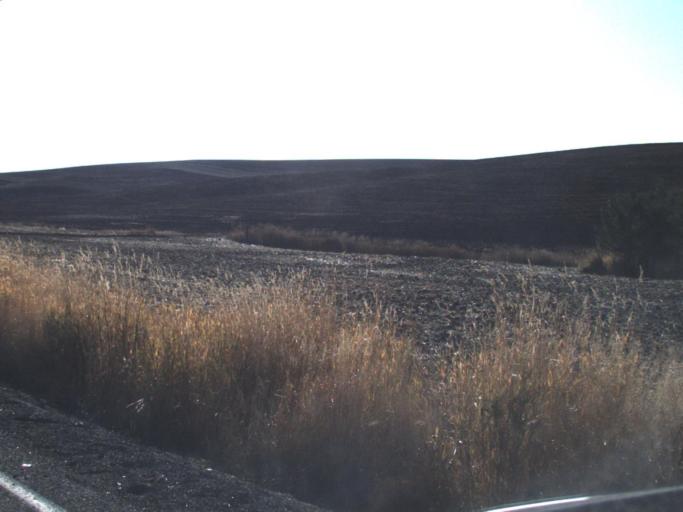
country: US
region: Washington
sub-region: Whitman County
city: Pullman
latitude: 46.7110
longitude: -117.2744
